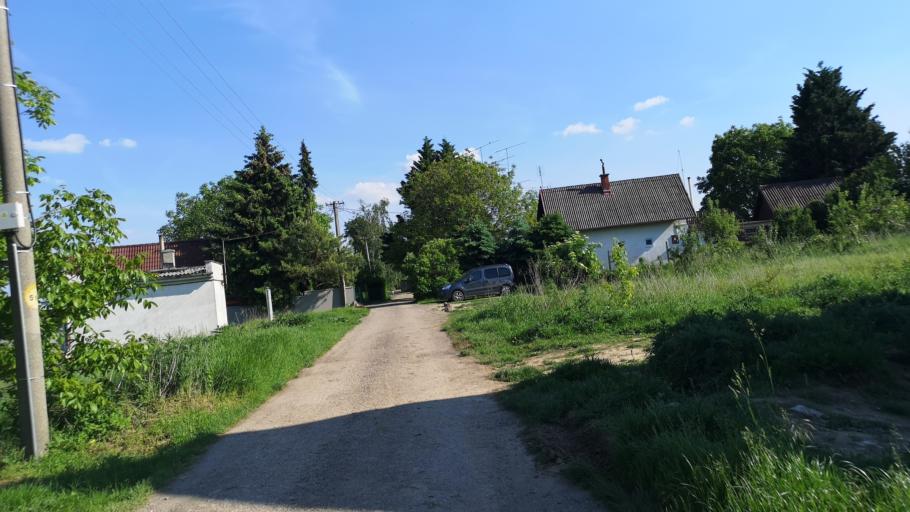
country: SK
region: Nitriansky
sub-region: Okres Nitra
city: Nitra
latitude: 48.2562
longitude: 18.0821
